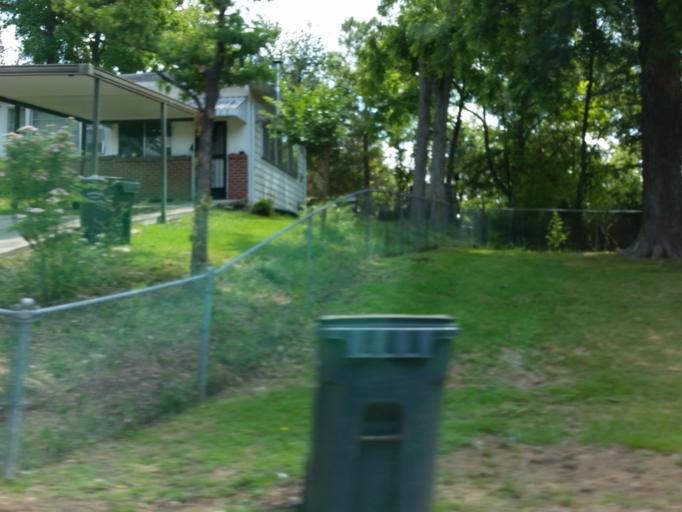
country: US
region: Mississippi
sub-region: Lauderdale County
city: Meridian
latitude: 32.3709
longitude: -88.7139
